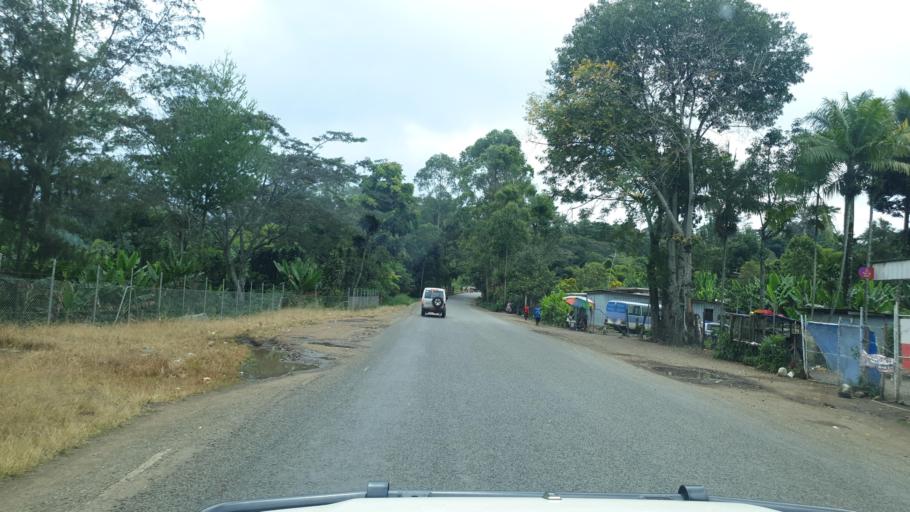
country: PG
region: Eastern Highlands
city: Goroka
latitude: -6.0450
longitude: 145.3756
